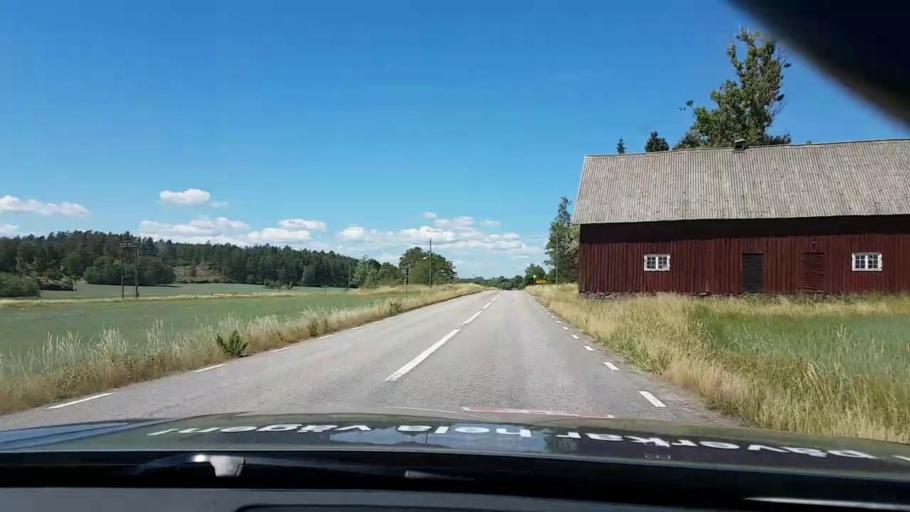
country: SE
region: Kalmar
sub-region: Vasterviks Kommun
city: Forserum
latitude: 57.9339
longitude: 16.5070
